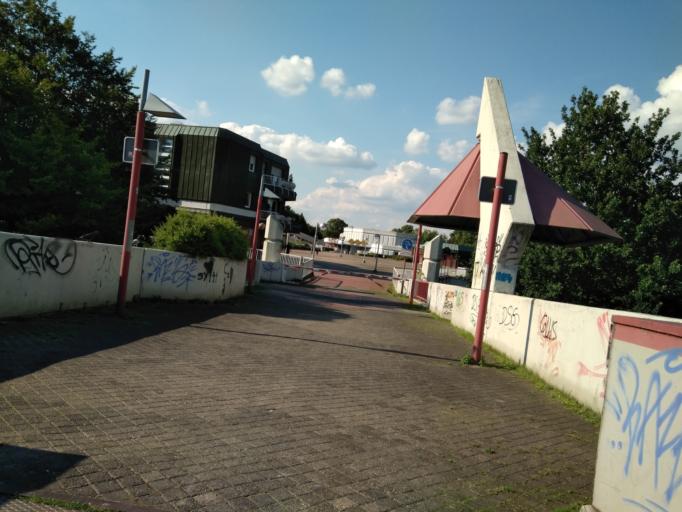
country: DE
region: North Rhine-Westphalia
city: Dorsten
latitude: 51.6644
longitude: 6.9639
